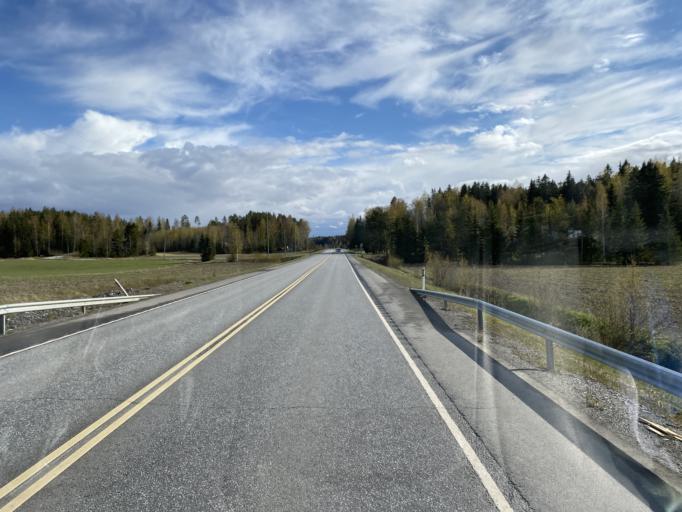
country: FI
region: Pirkanmaa
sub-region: Tampere
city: Lempaeaelae
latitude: 61.2657
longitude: 23.7450
